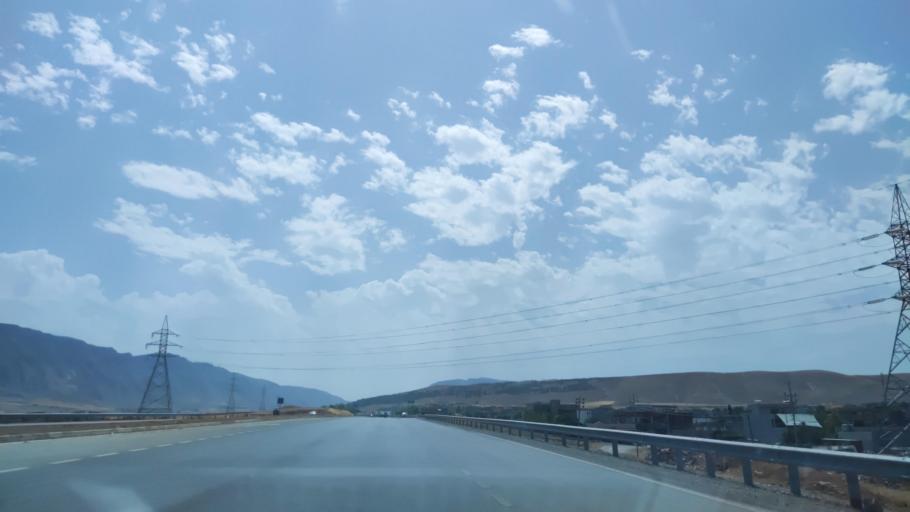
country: IQ
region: Arbil
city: Shaqlawah
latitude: 36.5070
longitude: 44.3489
